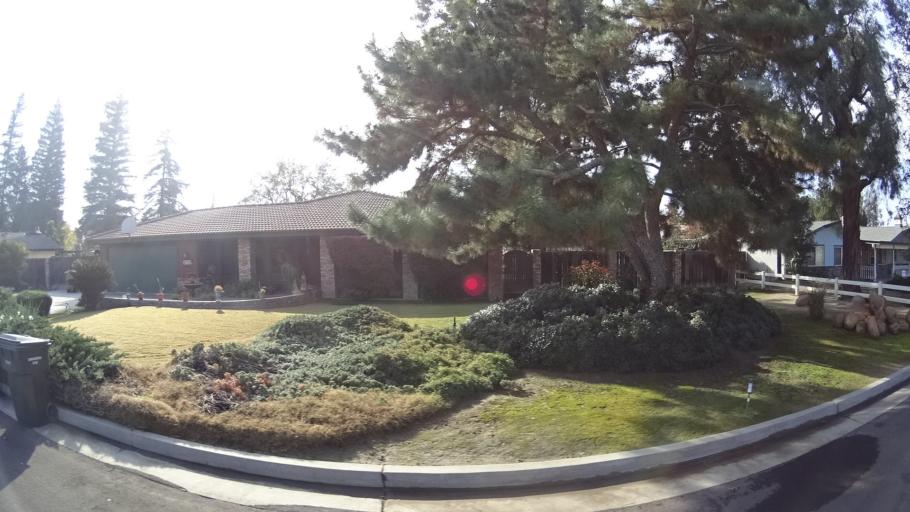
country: US
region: California
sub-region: Kern County
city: Rosedale
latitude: 35.3671
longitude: -119.1513
